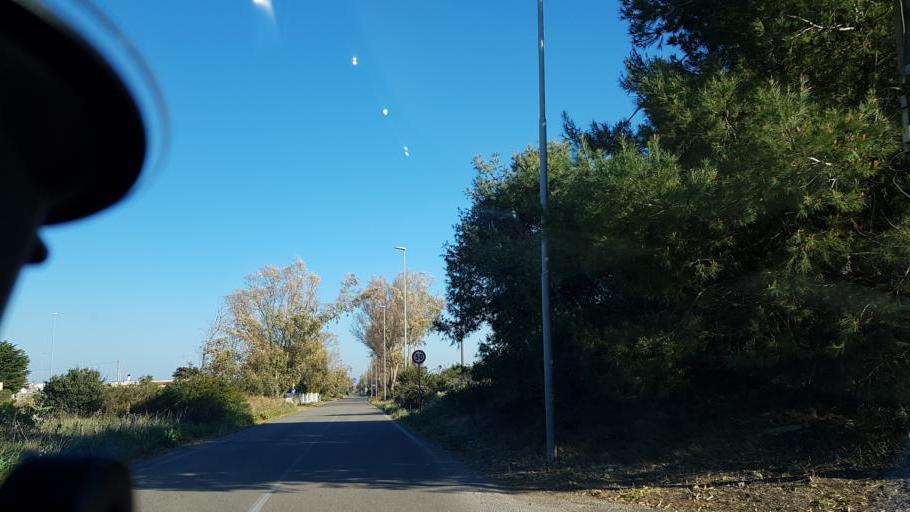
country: IT
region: Apulia
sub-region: Provincia di Lecce
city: Giorgilorio
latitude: 40.4544
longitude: 18.2150
